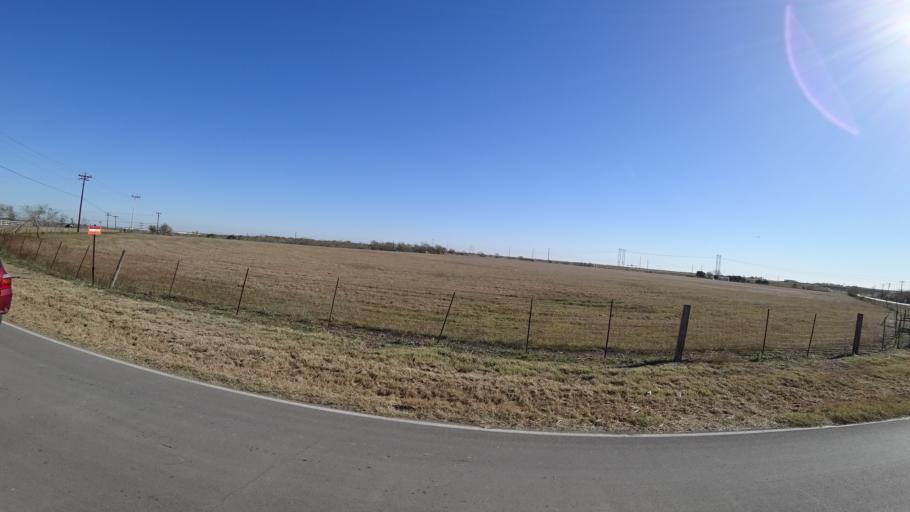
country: US
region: Texas
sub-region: Travis County
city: Onion Creek
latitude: 30.0974
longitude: -97.6845
